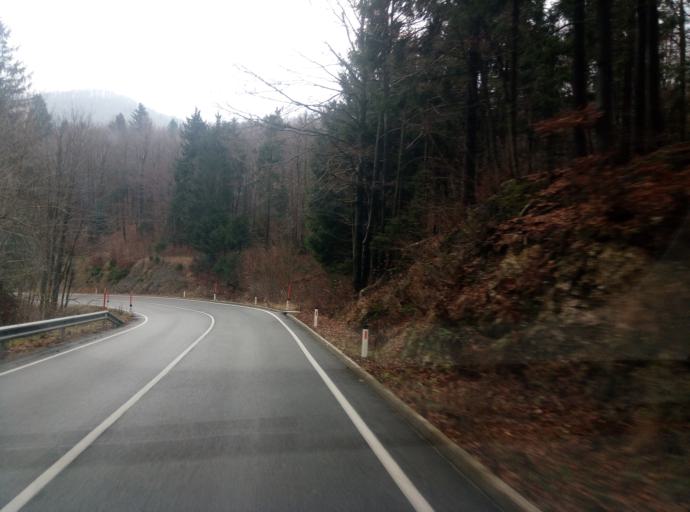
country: SI
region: Idrija
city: Idrija
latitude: 45.9237
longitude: 14.0366
